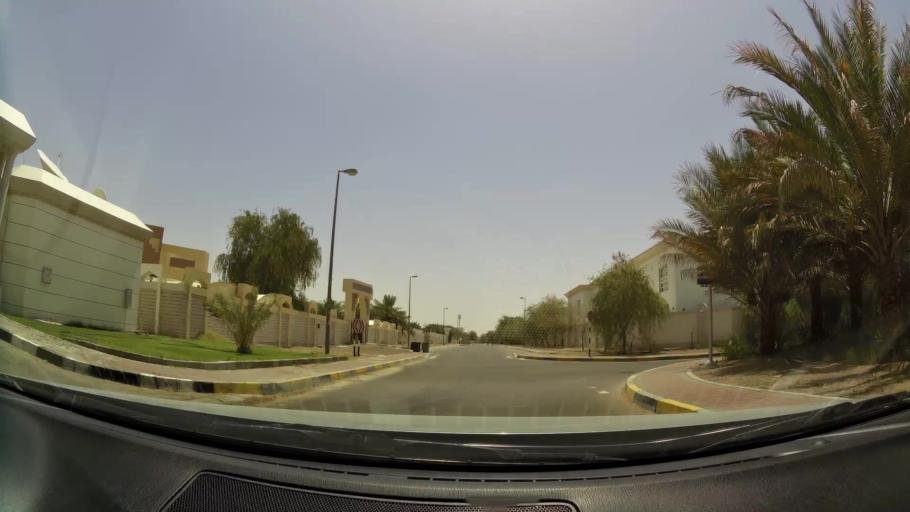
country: OM
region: Al Buraimi
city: Al Buraymi
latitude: 24.2837
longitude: 55.7565
